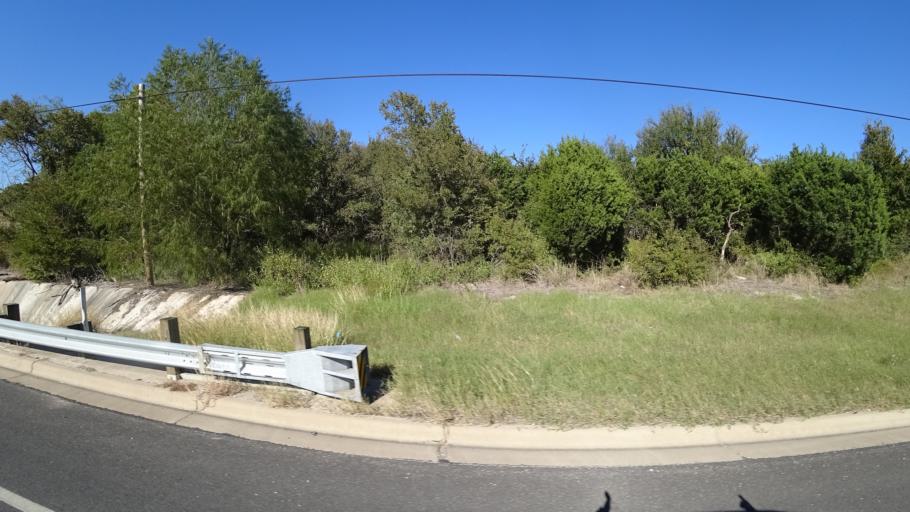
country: US
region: Texas
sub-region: Travis County
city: Hornsby Bend
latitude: 30.2789
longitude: -97.6427
